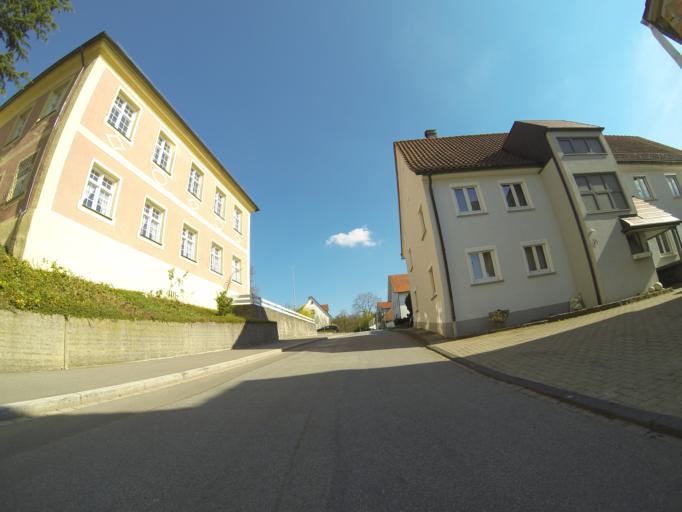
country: DE
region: Baden-Wuerttemberg
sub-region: Tuebingen Region
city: Laupheim
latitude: 48.2293
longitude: 9.8868
